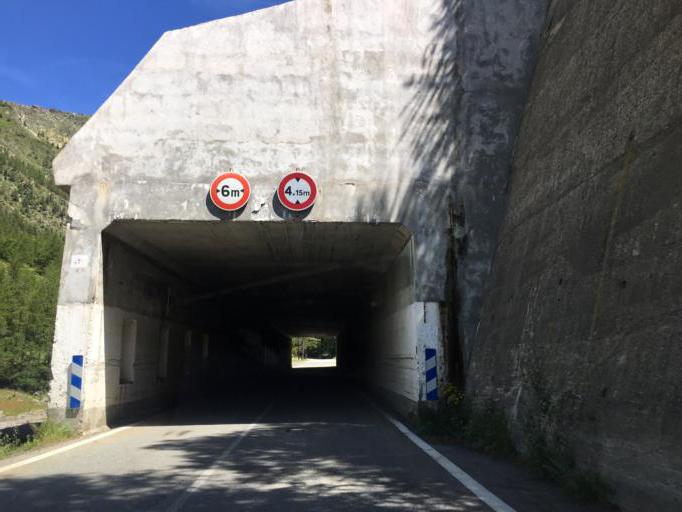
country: IT
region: Piedmont
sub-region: Provincia di Cuneo
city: Vinadio
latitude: 44.2044
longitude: 7.0965
